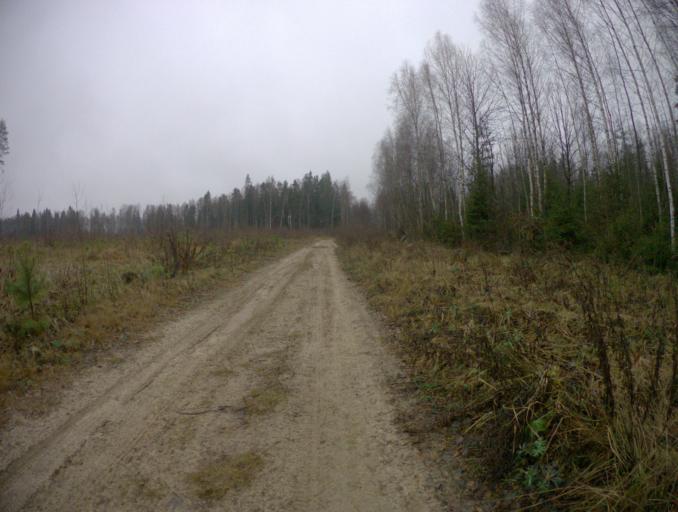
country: RU
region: Vladimir
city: Golovino
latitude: 55.9913
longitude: 40.4475
